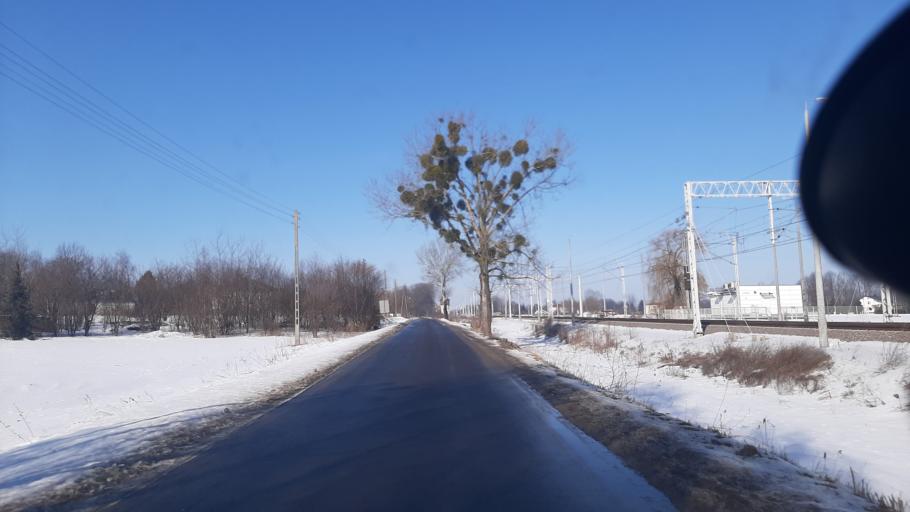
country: PL
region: Lublin Voivodeship
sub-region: Powiat lubelski
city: Wojciechow
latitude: 51.2817
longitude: 22.2913
